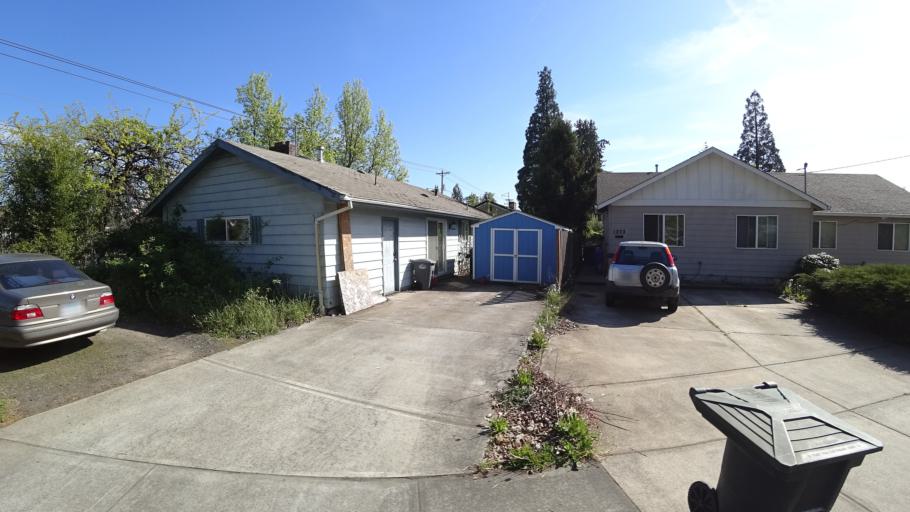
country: US
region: Oregon
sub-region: Washington County
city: Hillsboro
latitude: 45.5276
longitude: -122.9694
